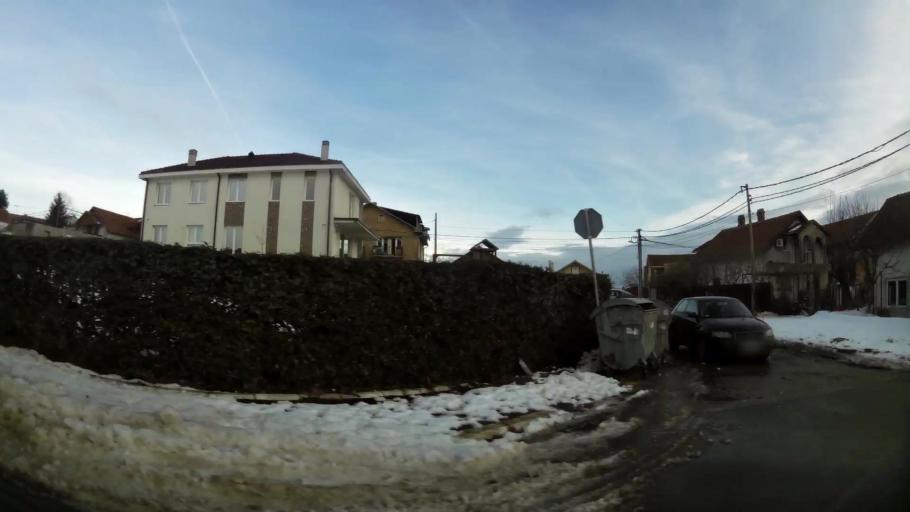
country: RS
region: Central Serbia
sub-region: Belgrade
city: Zvezdara
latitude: 44.7364
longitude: 20.5131
